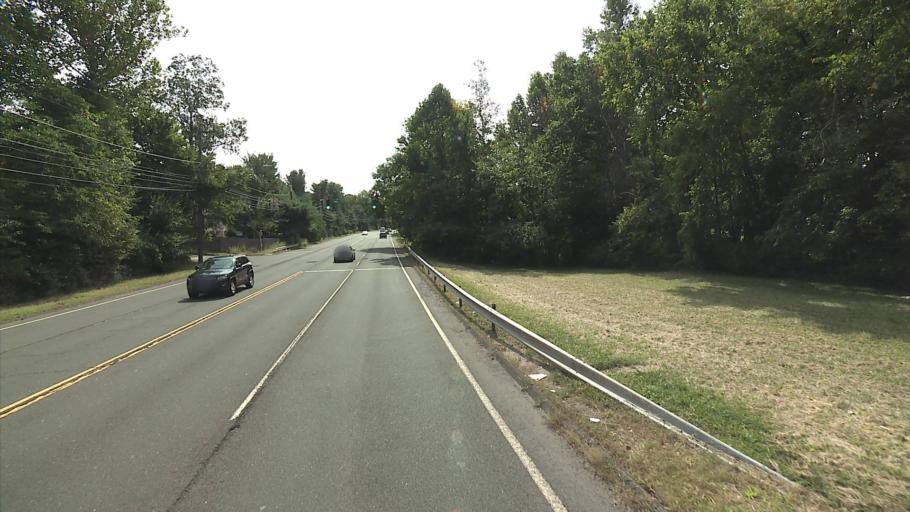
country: US
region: Connecticut
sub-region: Fairfield County
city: Stamford
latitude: 41.0845
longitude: -73.5557
